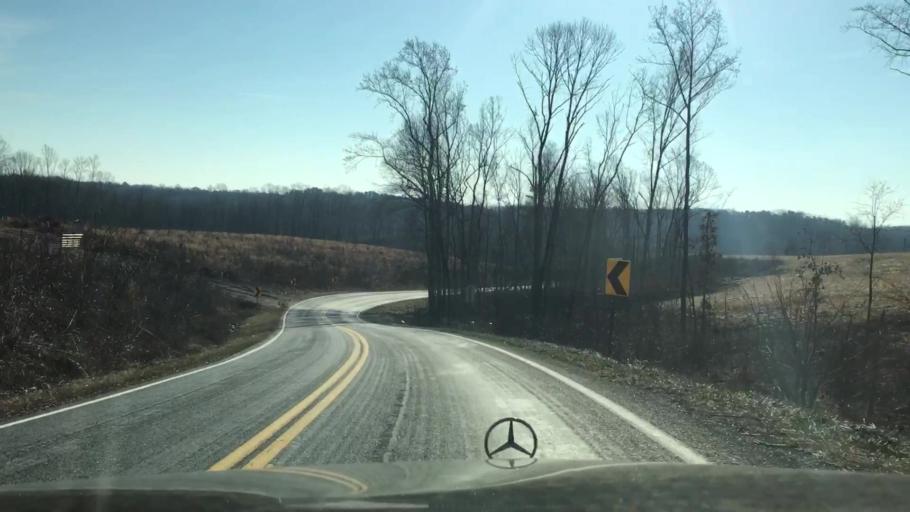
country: US
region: Virginia
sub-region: Campbell County
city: Altavista
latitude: 37.1516
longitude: -79.3392
